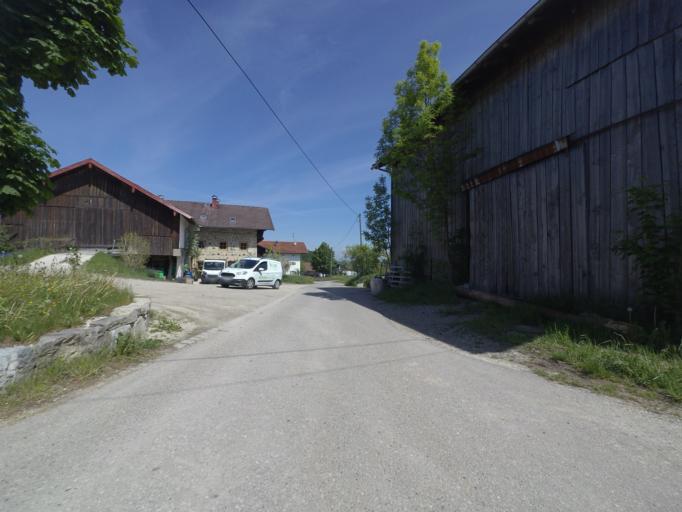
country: DE
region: Bavaria
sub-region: Upper Bavaria
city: Petting
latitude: 47.9048
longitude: 12.8001
